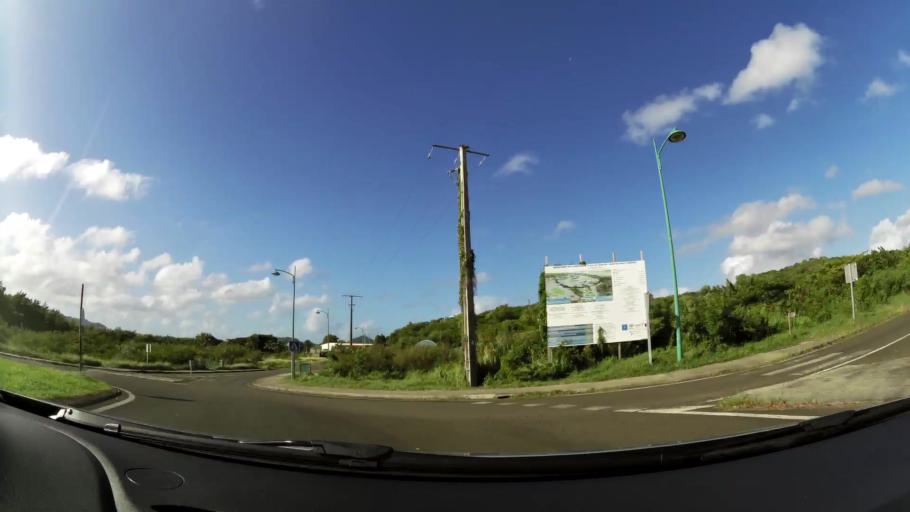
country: MQ
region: Martinique
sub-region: Martinique
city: Le Francois
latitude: 14.6216
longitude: -60.9035
